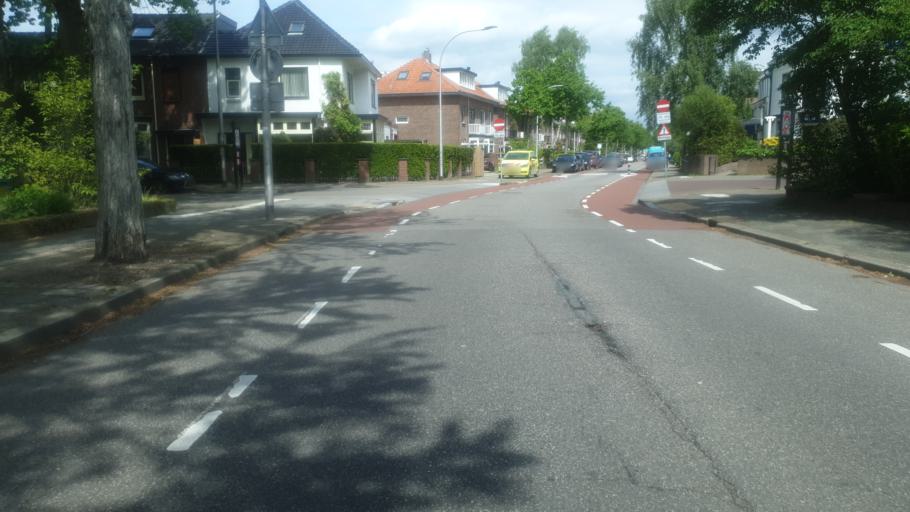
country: NL
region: Gelderland
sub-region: Gemeente Nijmegen
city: Nijmegen
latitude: 51.8266
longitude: 5.8472
